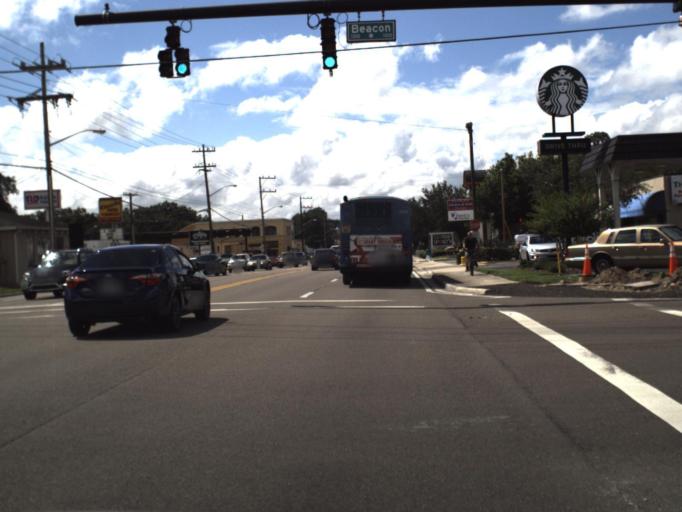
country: US
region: Florida
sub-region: Polk County
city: Lakeland
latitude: 28.0187
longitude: -81.9572
